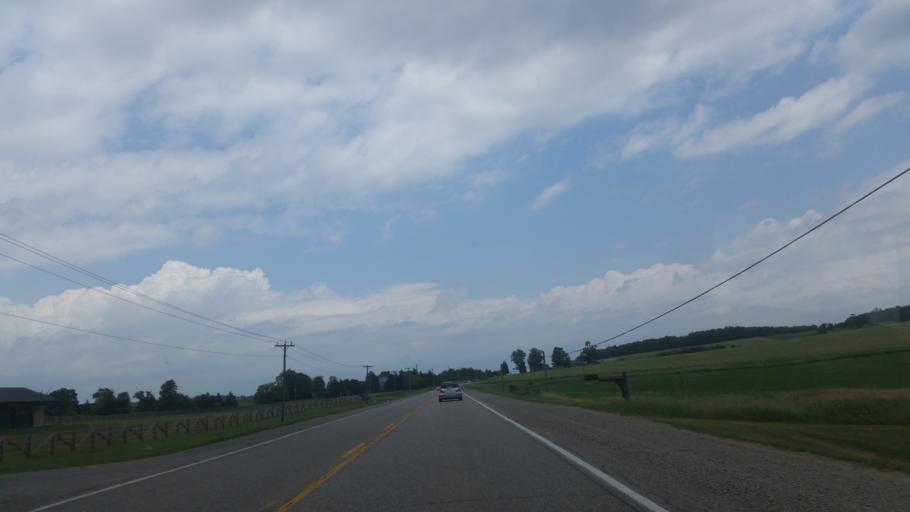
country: CA
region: Ontario
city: Orangeville
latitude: 43.7253
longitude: -80.1043
